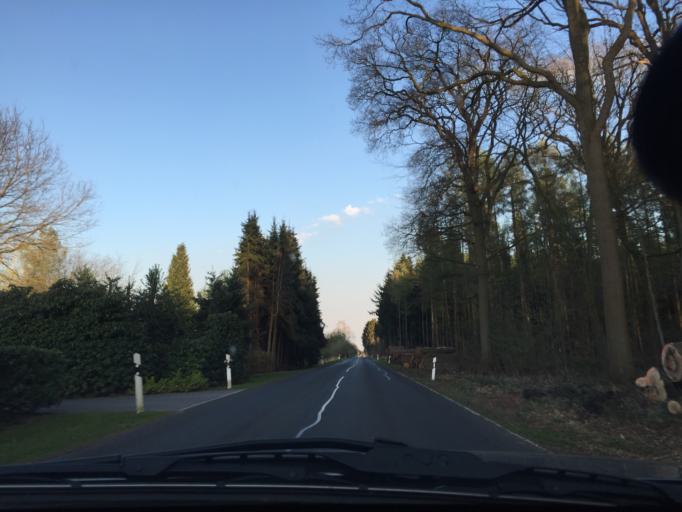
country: DE
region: North Rhine-Westphalia
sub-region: Regierungsbezirk Dusseldorf
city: Kleve
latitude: 51.7441
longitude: 6.1367
